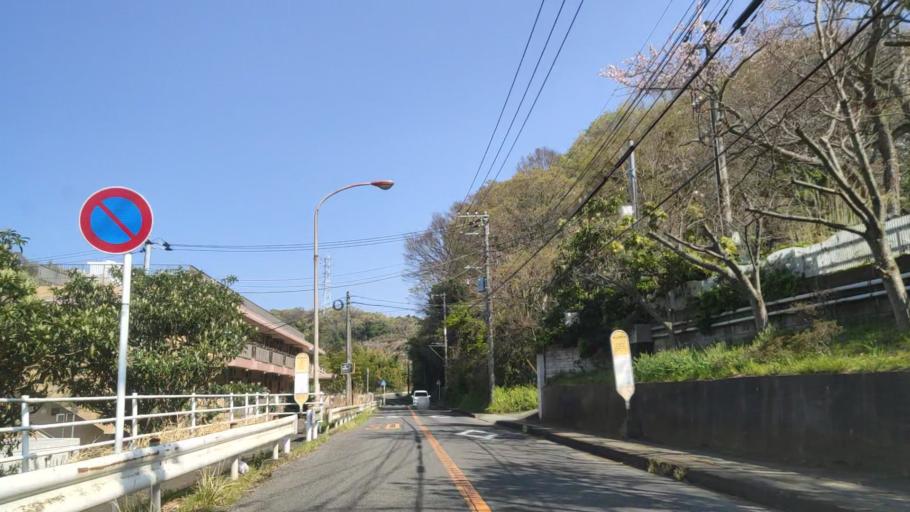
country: JP
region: Kanagawa
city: Ninomiya
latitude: 35.3157
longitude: 139.2730
